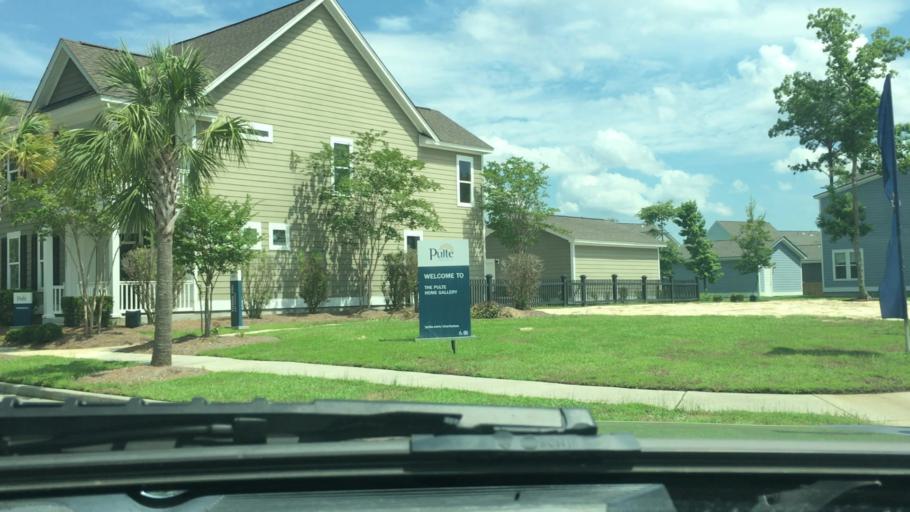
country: US
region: South Carolina
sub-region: Charleston County
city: Shell Point
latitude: 32.8085
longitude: -80.0739
